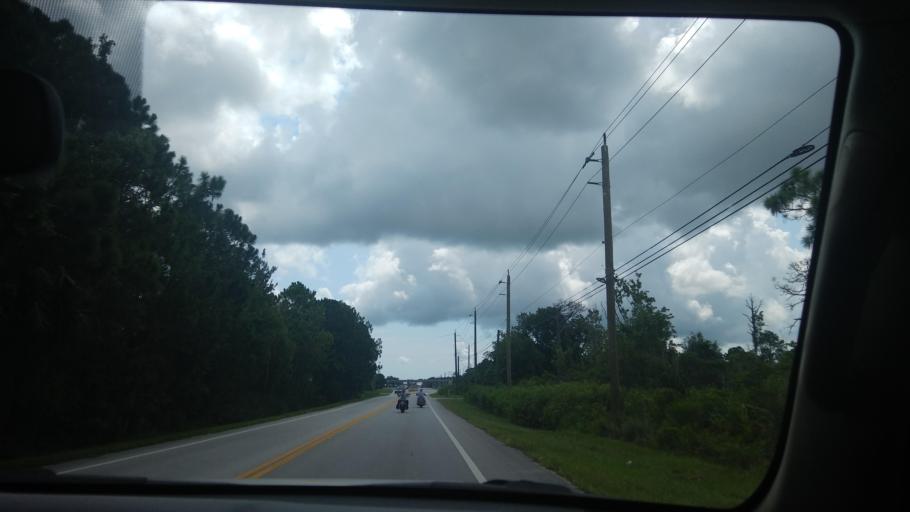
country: US
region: Florida
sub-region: Indian River County
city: Fellsmere
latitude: 27.7676
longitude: -80.5583
